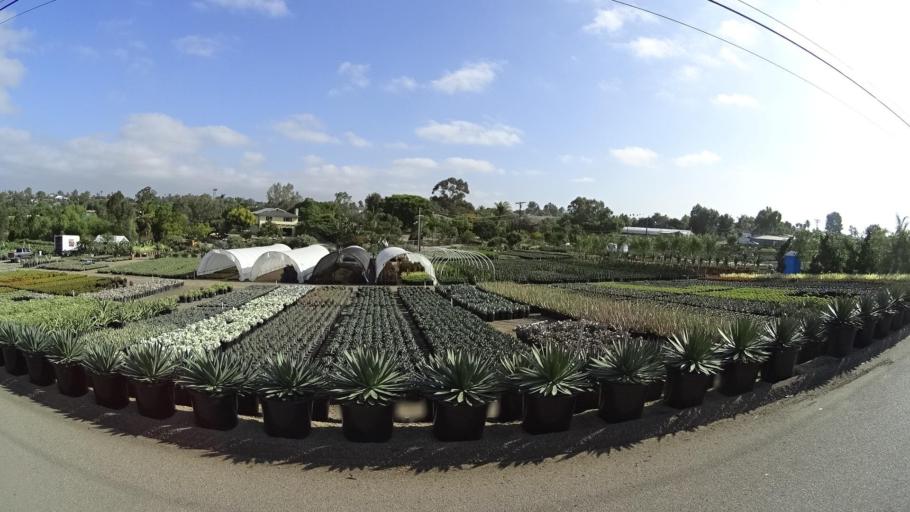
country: US
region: California
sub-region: San Diego County
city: Vista
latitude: 33.1712
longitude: -117.2476
